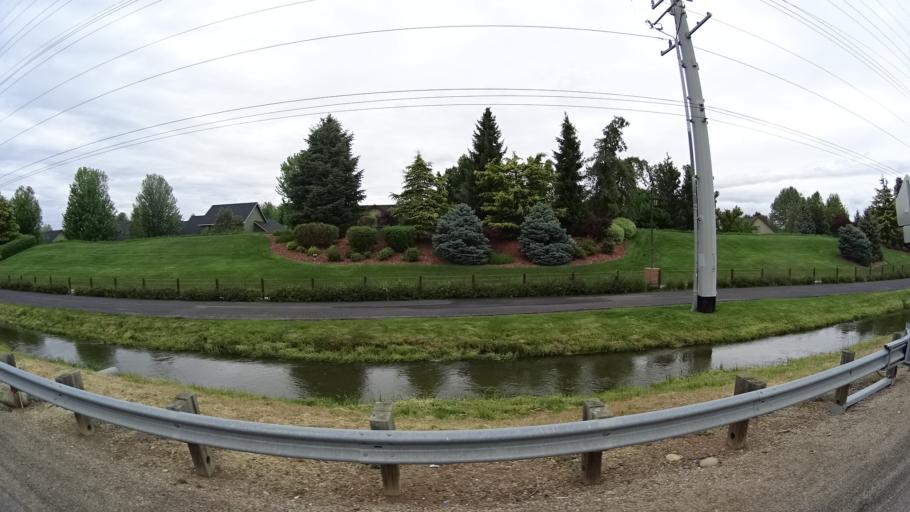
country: US
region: Idaho
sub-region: Ada County
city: Meridian
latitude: 43.6484
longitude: -116.3830
